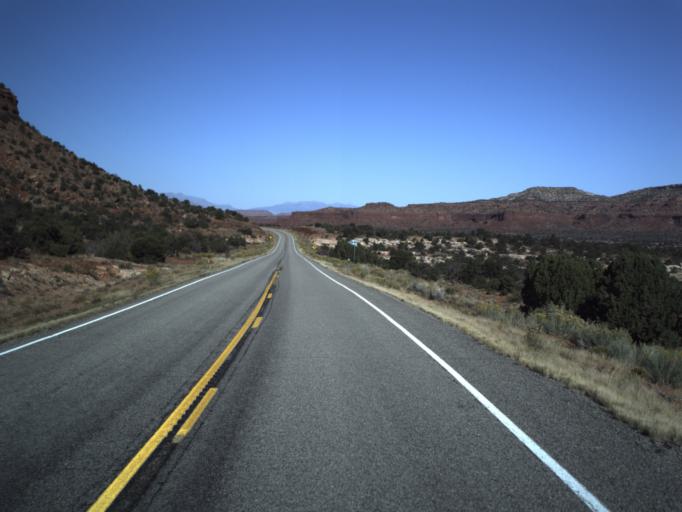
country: US
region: Utah
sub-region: San Juan County
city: Blanding
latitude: 37.6473
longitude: -110.1155
